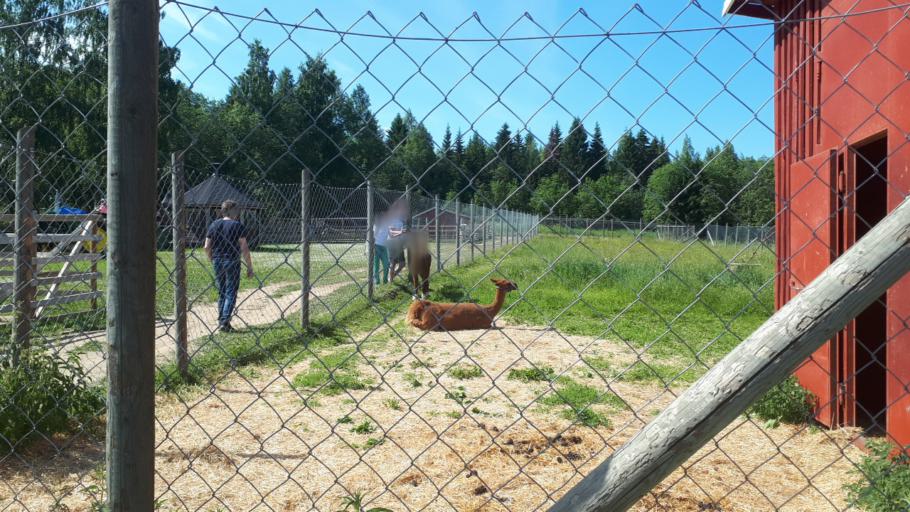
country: FI
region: Northern Savo
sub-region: Kuopio
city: Kuopio
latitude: 62.7519
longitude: 27.5515
